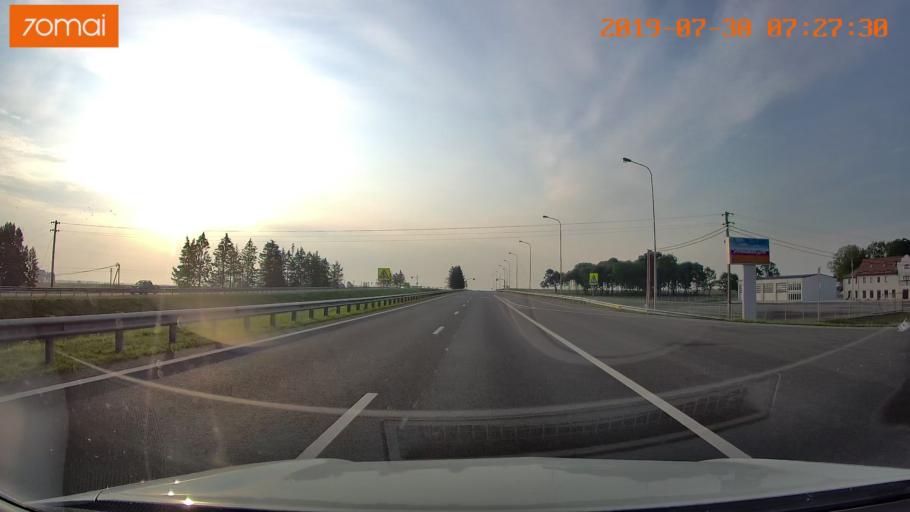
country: RU
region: Kaliningrad
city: Gvardeysk
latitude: 54.6819
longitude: 20.8889
